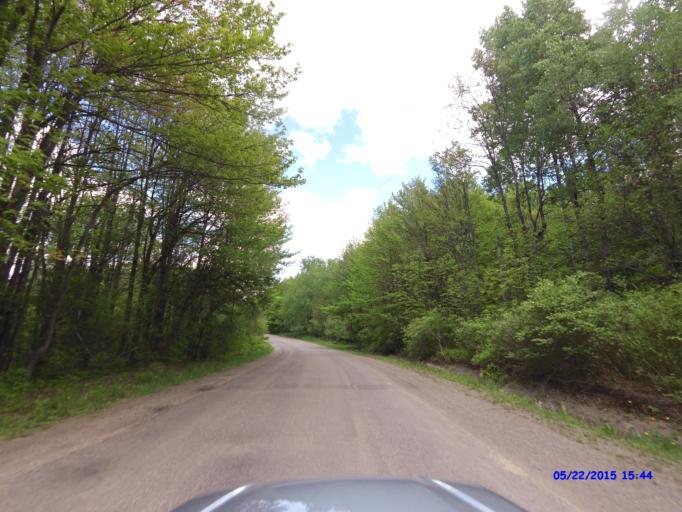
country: US
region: New York
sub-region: Cattaraugus County
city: Franklinville
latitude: 42.3124
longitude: -78.5471
